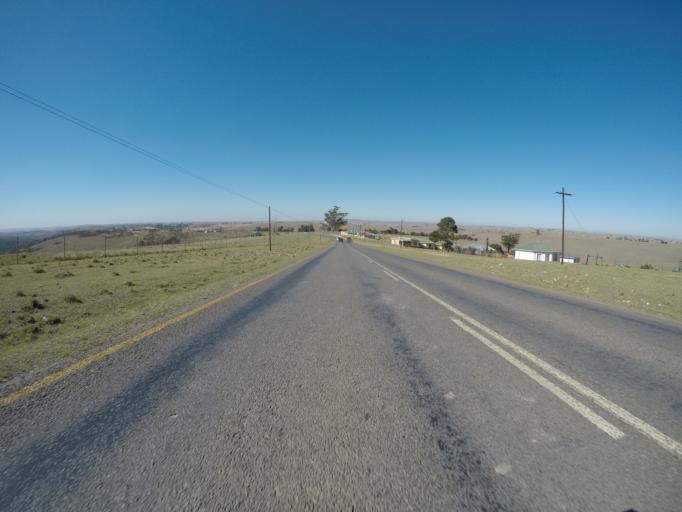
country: ZA
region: Eastern Cape
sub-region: OR Tambo District Municipality
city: Mthatha
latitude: -31.7941
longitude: 28.7450
